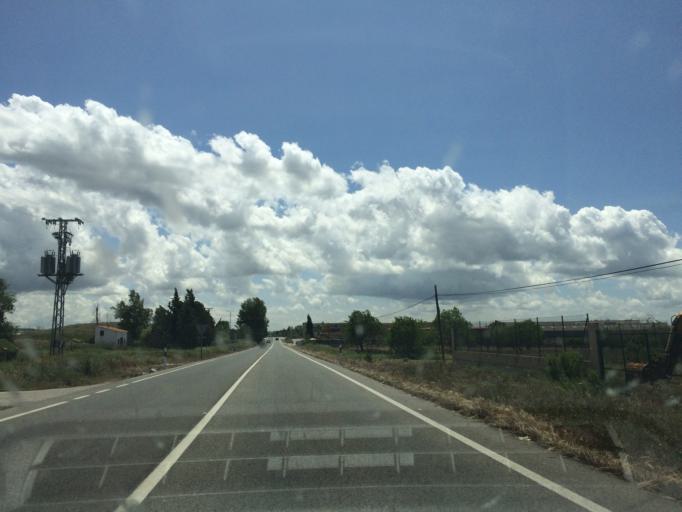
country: ES
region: Madrid
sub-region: Provincia de Madrid
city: Fuente el Saz
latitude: 40.6496
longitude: -3.5109
